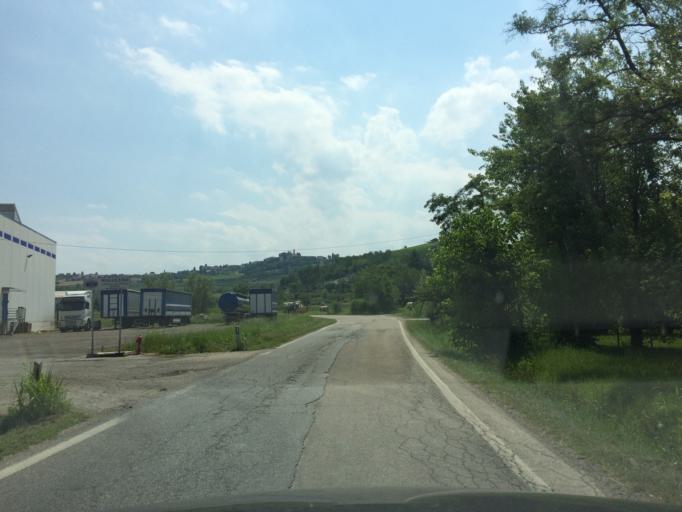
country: IT
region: Piedmont
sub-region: Provincia di Asti
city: San Marzano Oliveto
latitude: 44.7670
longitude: 8.3070
